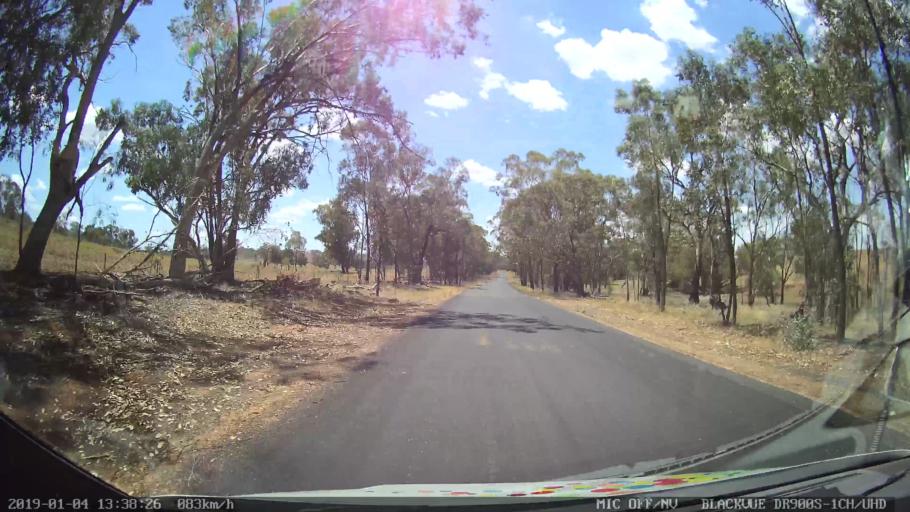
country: AU
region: New South Wales
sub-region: Dubbo Municipality
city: Dubbo
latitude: -32.5381
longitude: 148.5475
